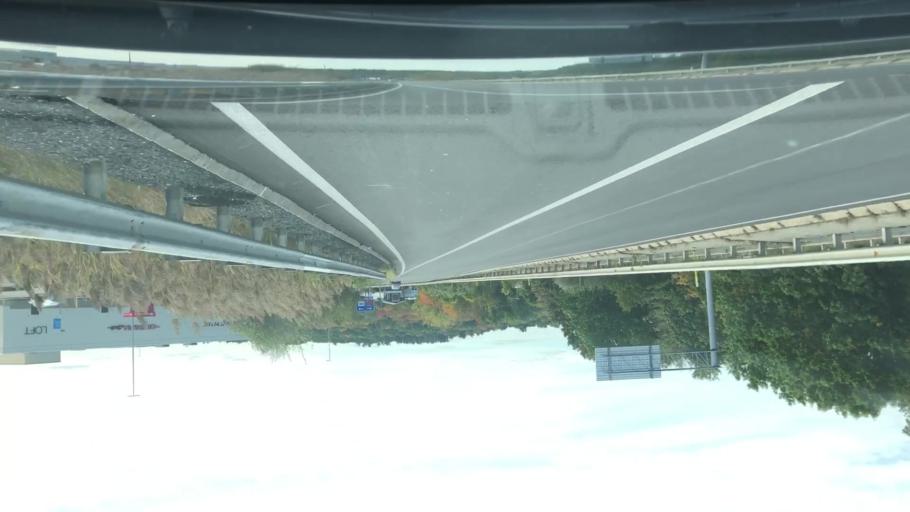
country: US
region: Massachusetts
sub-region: Essex County
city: Lawrence
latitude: 42.7451
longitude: -71.1558
